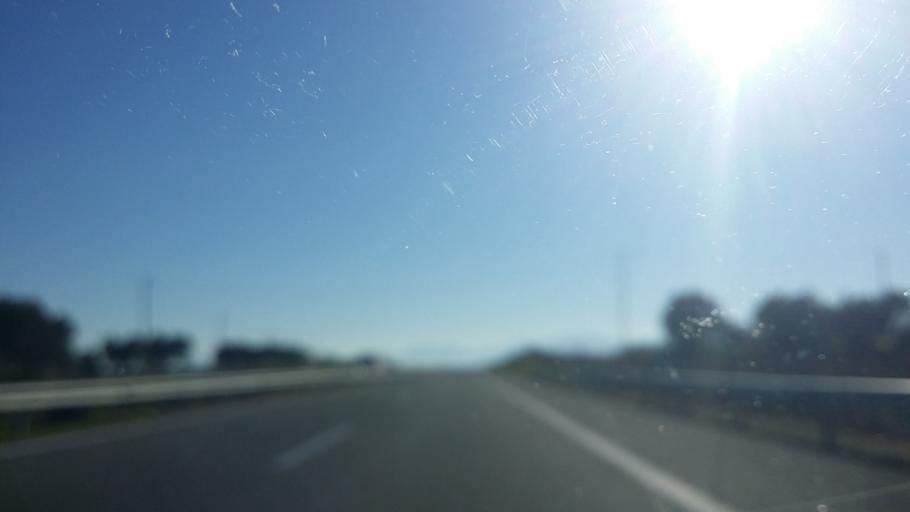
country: GR
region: West Greece
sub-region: Nomos Aitolias kai Akarnanias
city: Fitiai
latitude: 38.6700
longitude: 21.2304
